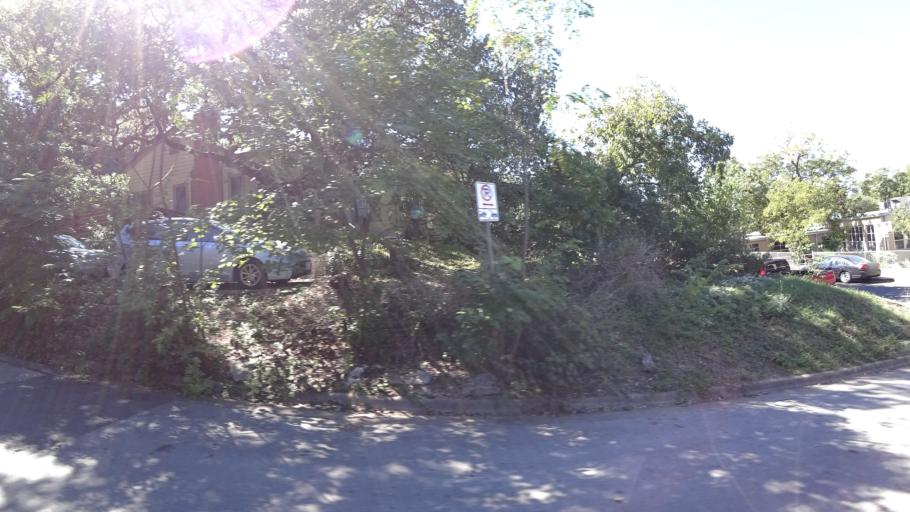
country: US
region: Texas
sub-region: Travis County
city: Austin
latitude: 30.2413
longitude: -97.7453
